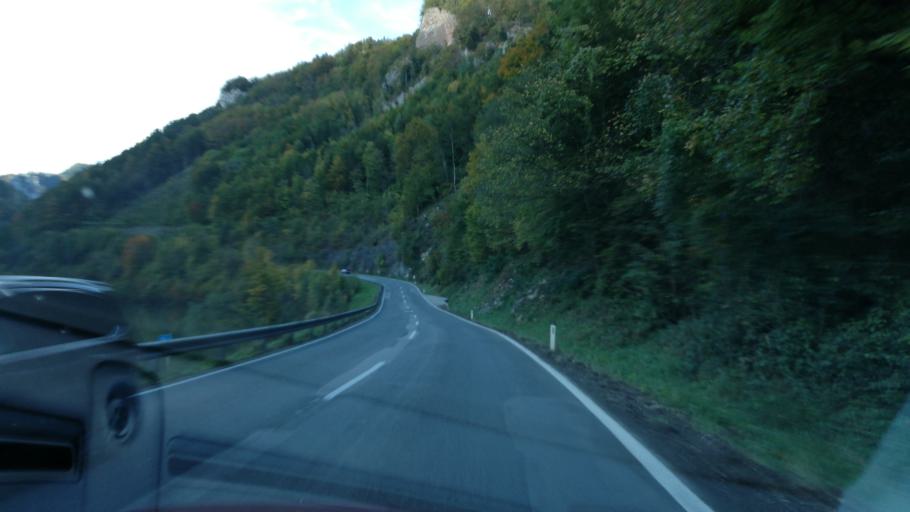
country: AT
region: Upper Austria
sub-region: Politischer Bezirk Steyr-Land
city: Weyer
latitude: 47.8350
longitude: 14.6447
